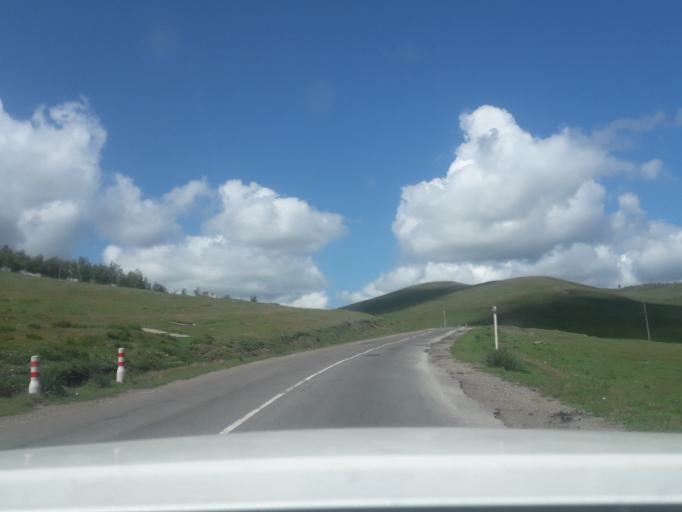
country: MN
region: Central Aimak
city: Ihsueuej
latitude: 48.1260
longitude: 106.4328
